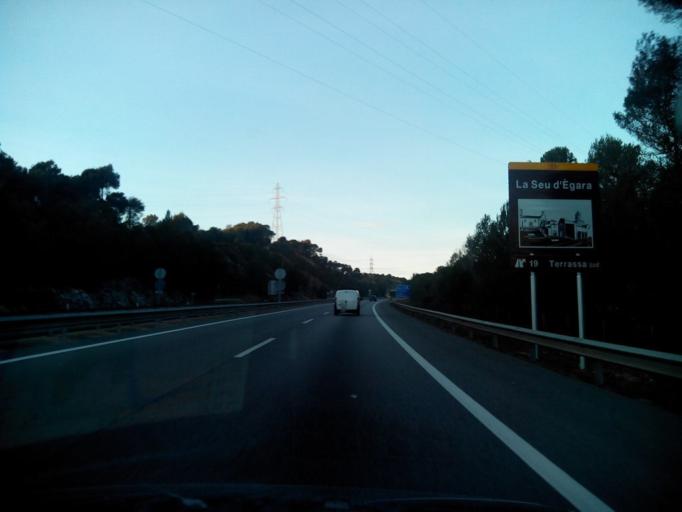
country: ES
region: Catalonia
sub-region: Provincia de Barcelona
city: Rubi
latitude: 41.5208
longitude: 2.0265
